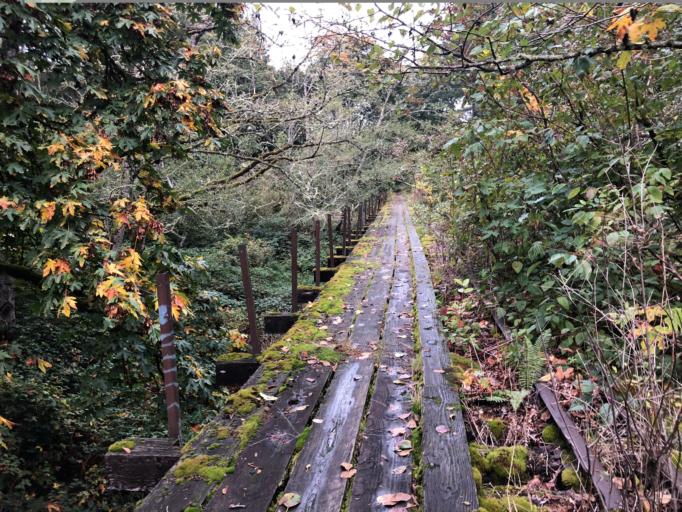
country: US
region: Washington
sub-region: King County
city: Snoqualmie
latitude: 47.5341
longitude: -121.8258
